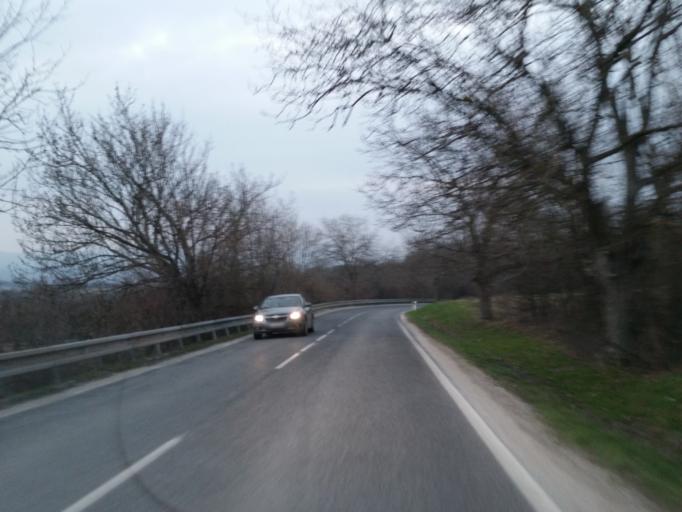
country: SK
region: Trnavsky
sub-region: Okres Trnava
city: Piestany
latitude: 48.5657
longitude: 17.8651
